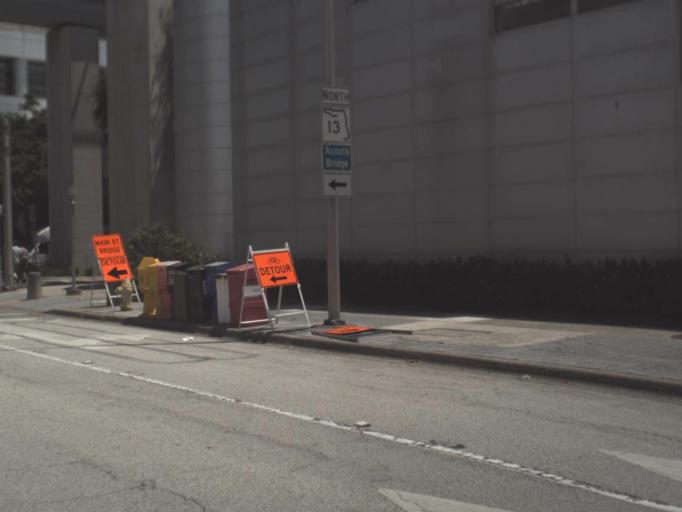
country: US
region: Florida
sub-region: Duval County
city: Jacksonville
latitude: 30.3174
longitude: -81.6605
